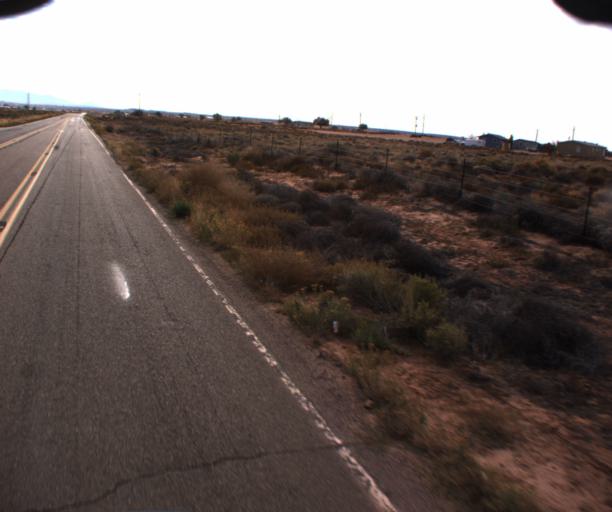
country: US
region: Arizona
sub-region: Apache County
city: Many Farms
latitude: 36.5146
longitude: -109.4816
